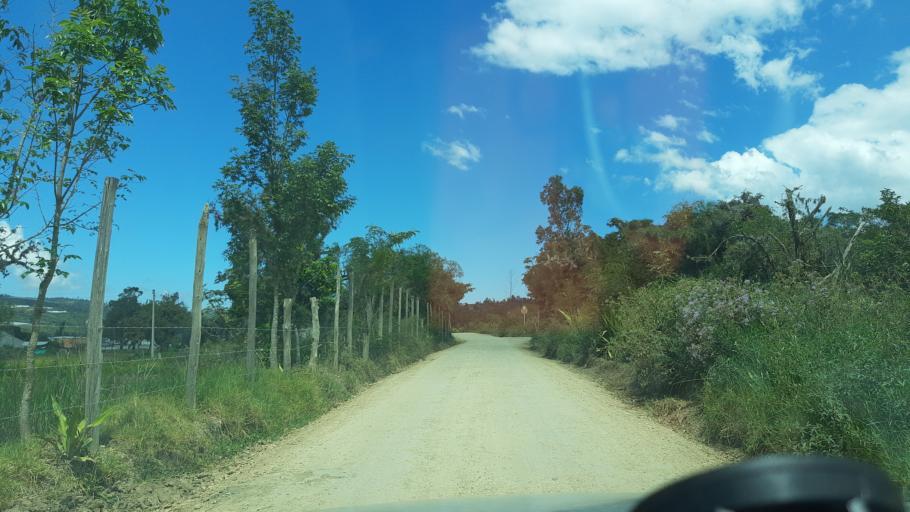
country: CO
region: Boyaca
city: Villa de Leiva
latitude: 5.6619
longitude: -73.5724
